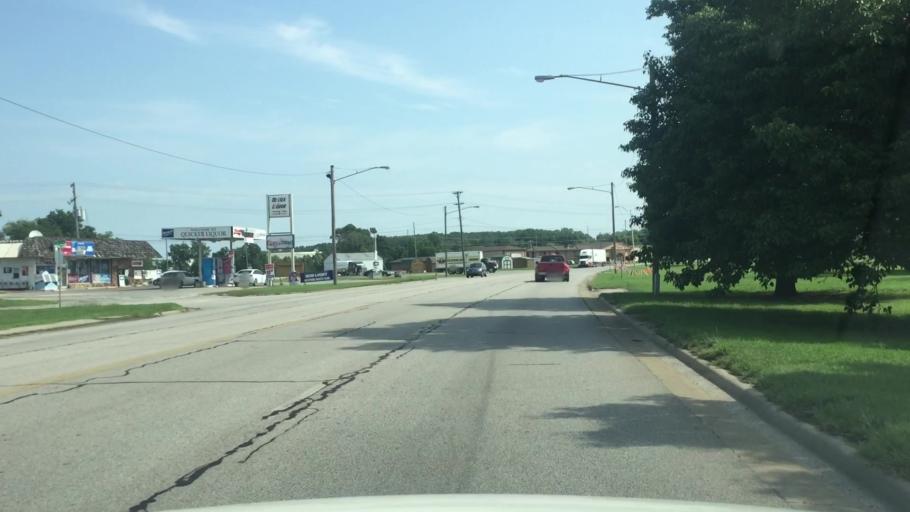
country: US
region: Kansas
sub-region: Montgomery County
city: Coffeyville
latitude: 37.0385
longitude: -95.5981
